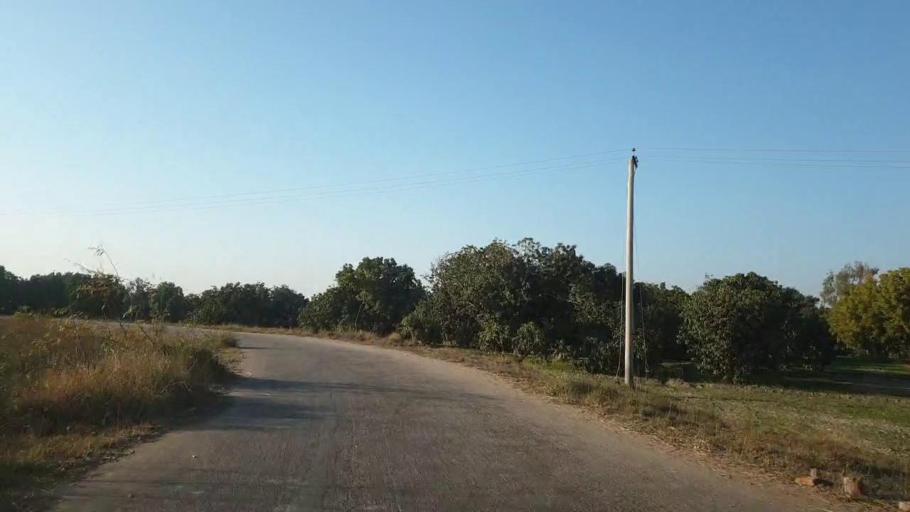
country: PK
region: Sindh
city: Mirpur Khas
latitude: 25.6567
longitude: 69.0964
